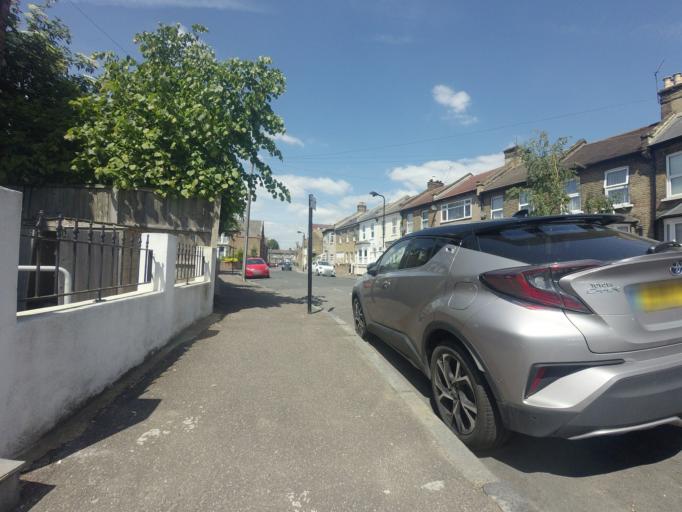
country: GB
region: England
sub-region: Greater London
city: East Ham
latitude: 51.5528
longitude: 0.0095
